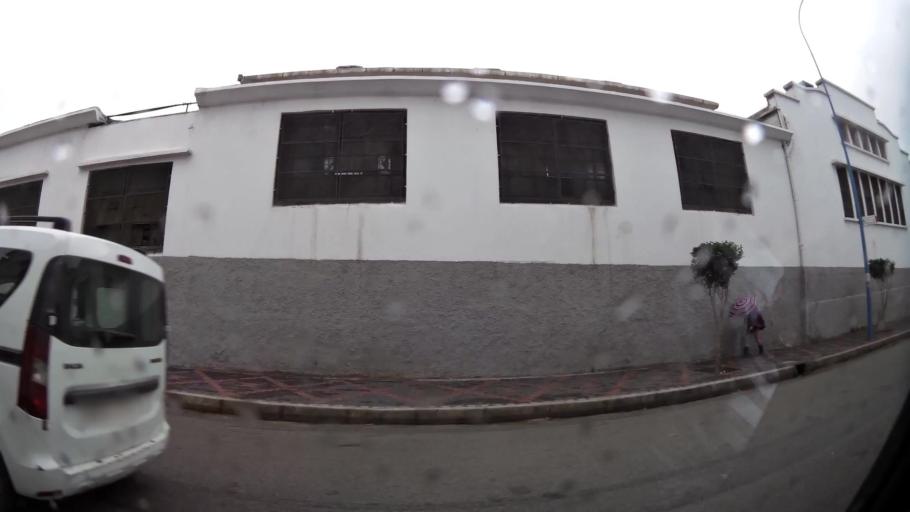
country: MA
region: Grand Casablanca
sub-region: Casablanca
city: Casablanca
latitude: 33.5807
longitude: -7.5972
